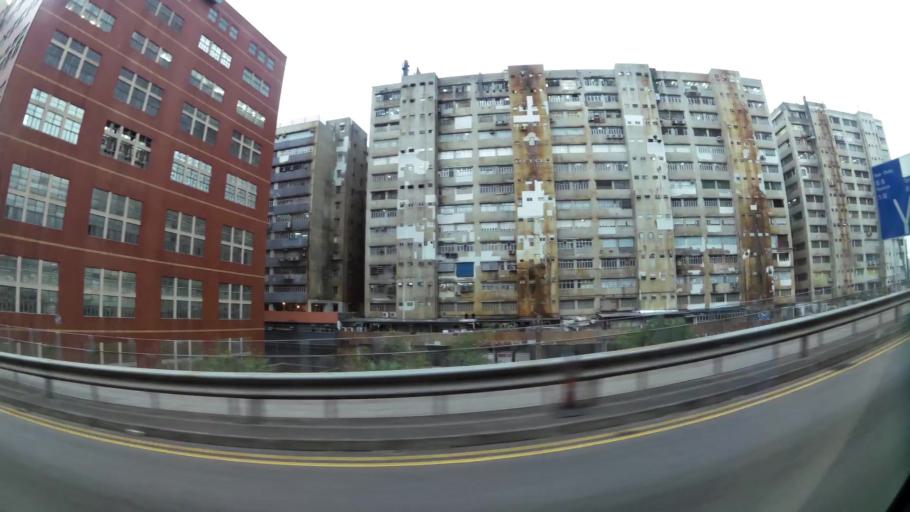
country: HK
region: Tsuen Wan
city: Tsuen Wan
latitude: 22.3496
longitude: 114.1096
